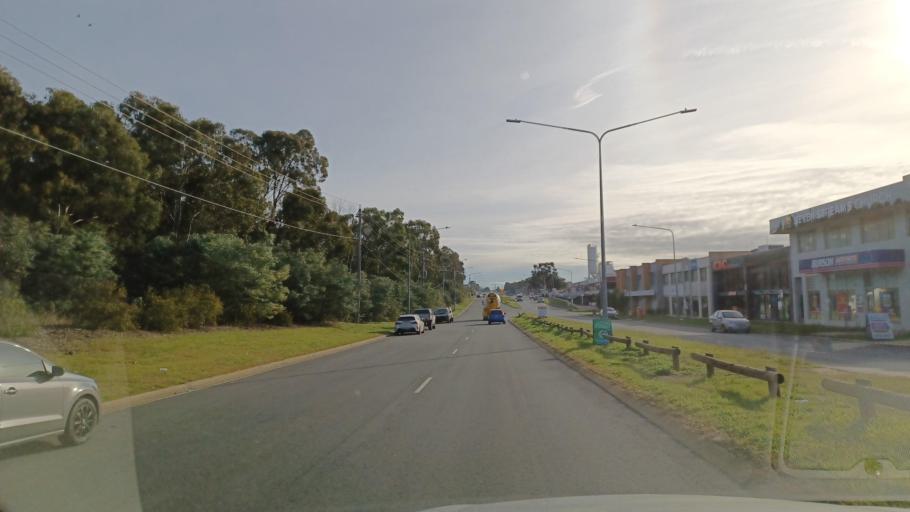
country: AU
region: Australian Capital Territory
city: Kaleen
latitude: -35.2164
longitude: 149.1372
